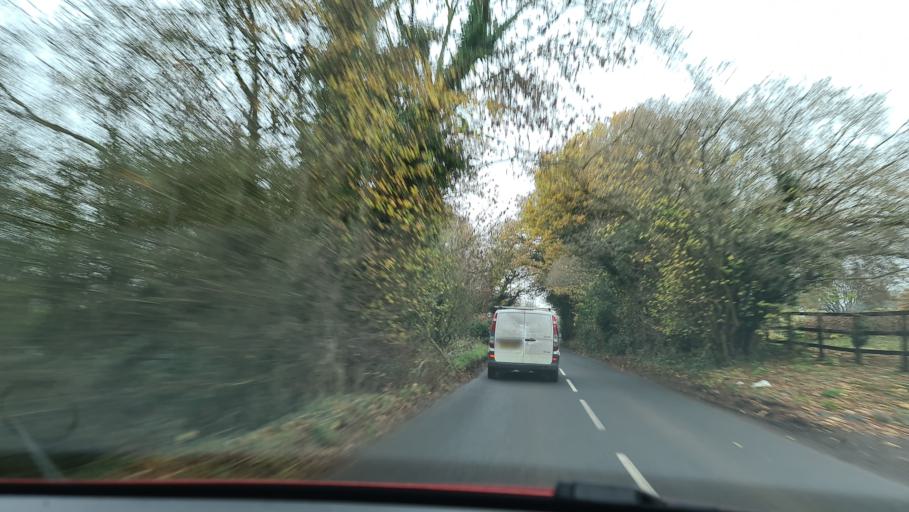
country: GB
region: England
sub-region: Buckinghamshire
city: Seer Green
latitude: 51.6213
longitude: -0.5901
